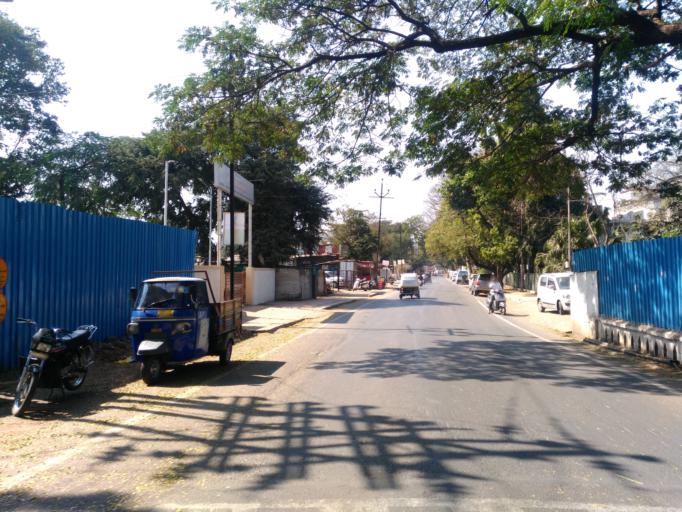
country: IN
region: Maharashtra
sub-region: Pune Division
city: Pune
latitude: 18.4785
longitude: 73.8598
